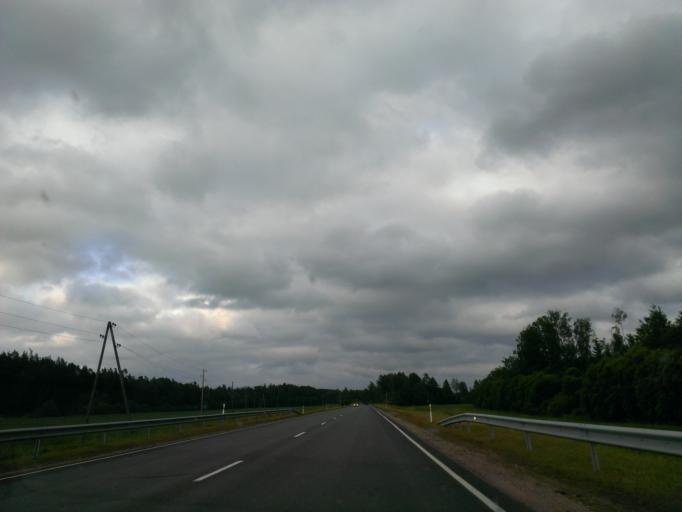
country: LV
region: Skrunda
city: Skrunda
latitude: 56.6782
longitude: 22.1419
